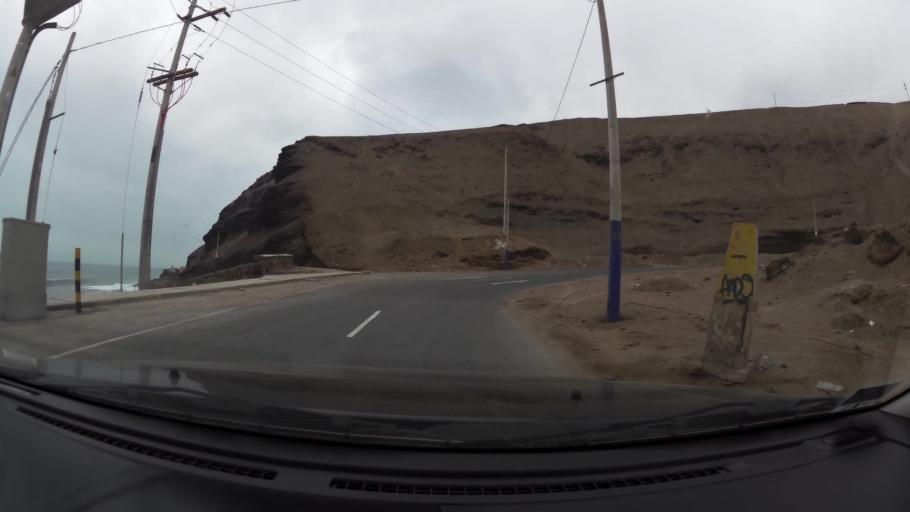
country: PE
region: Lima
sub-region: Lima
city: Surco
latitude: -12.1733
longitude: -77.0330
